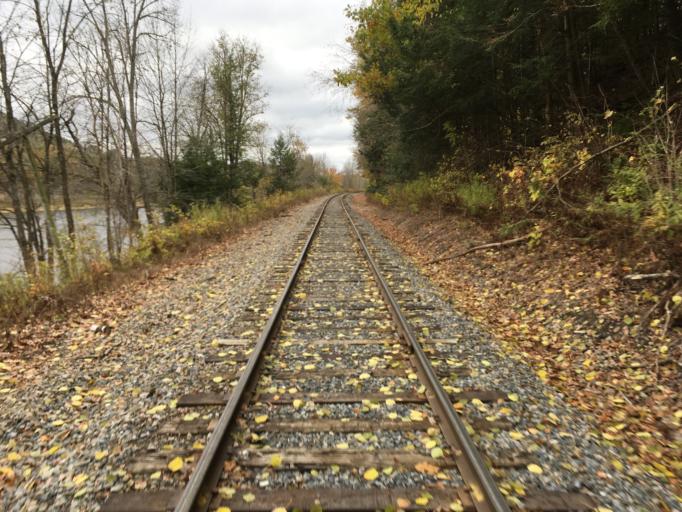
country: US
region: New Hampshire
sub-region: Grafton County
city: Woodsville
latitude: 44.1749
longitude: -72.0562
